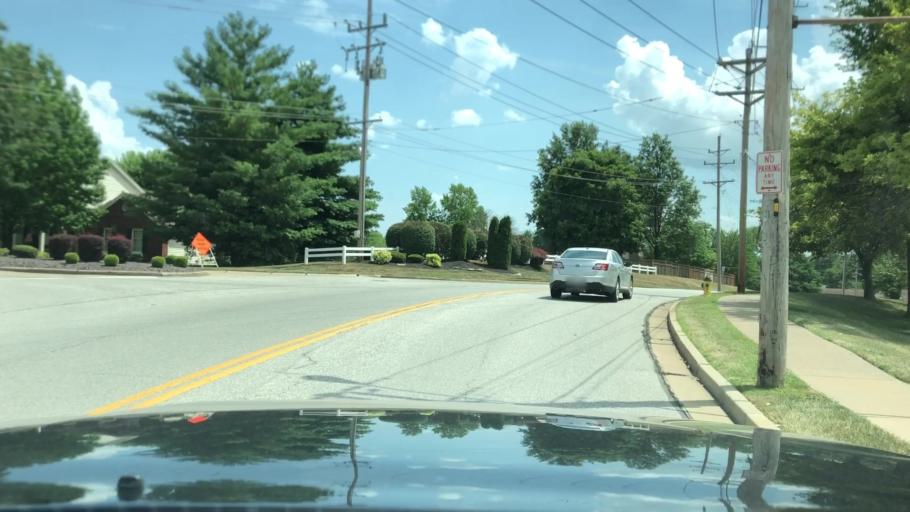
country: US
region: Missouri
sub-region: Saint Charles County
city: Saint Charles
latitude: 38.8018
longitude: -90.5310
